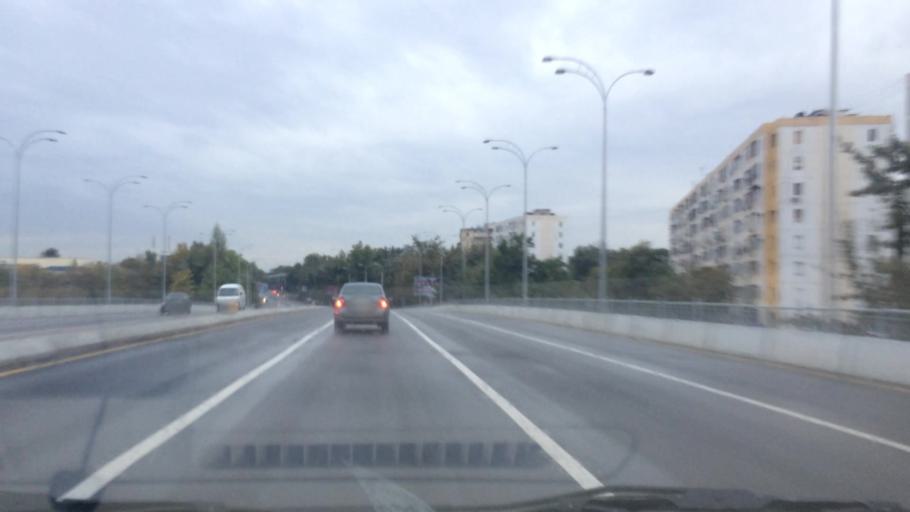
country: UZ
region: Toshkent Shahri
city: Tashkent
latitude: 41.2744
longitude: 69.2046
